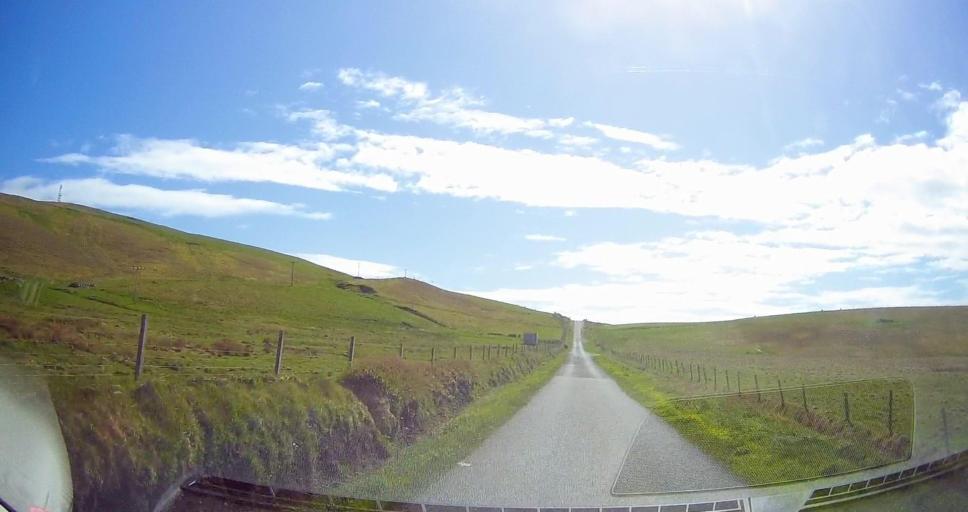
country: GB
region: Scotland
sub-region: Shetland Islands
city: Sandwick
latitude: 59.9644
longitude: -1.3216
